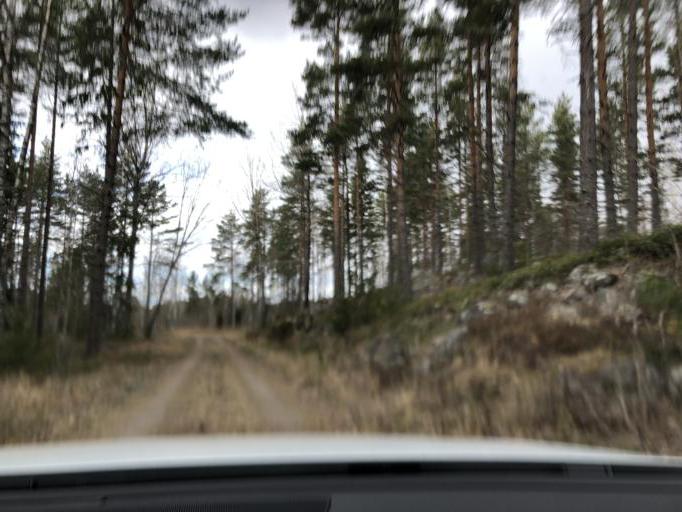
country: SE
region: Gaevleborg
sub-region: Gavle Kommun
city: Hedesunda
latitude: 60.3450
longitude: 17.0601
